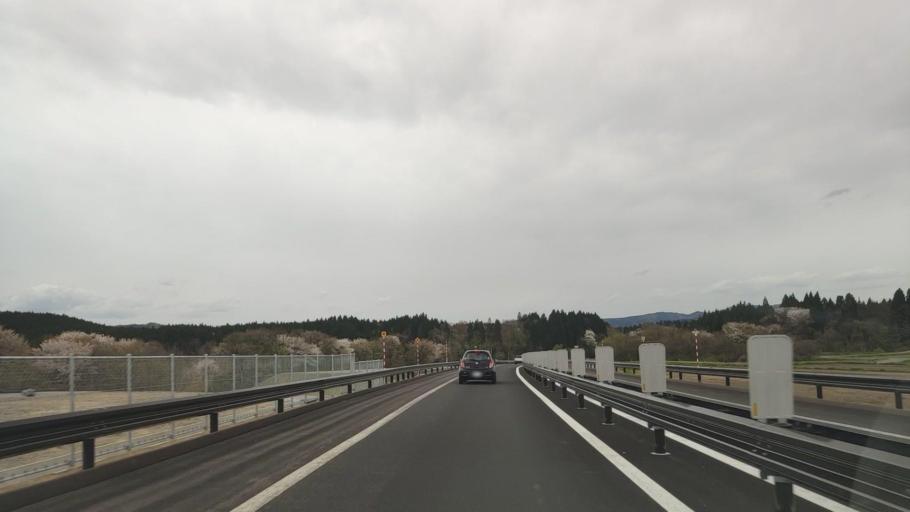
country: JP
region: Akita
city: Takanosu
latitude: 40.2003
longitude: 140.3573
